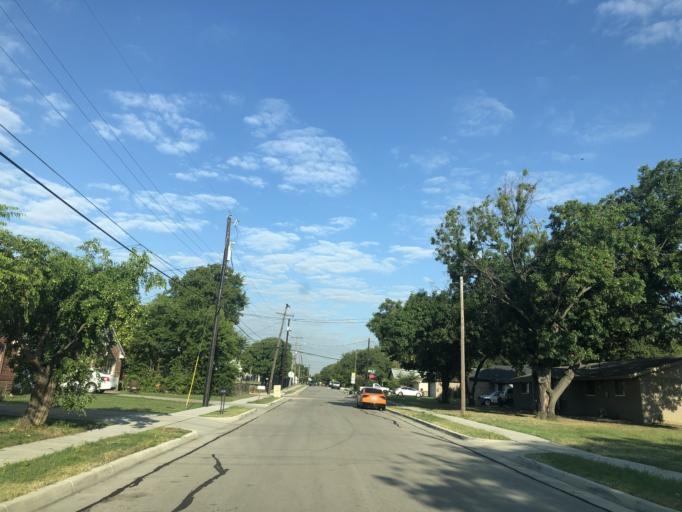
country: US
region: Texas
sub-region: Dallas County
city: Grand Prairie
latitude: 32.7341
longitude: -97.0284
